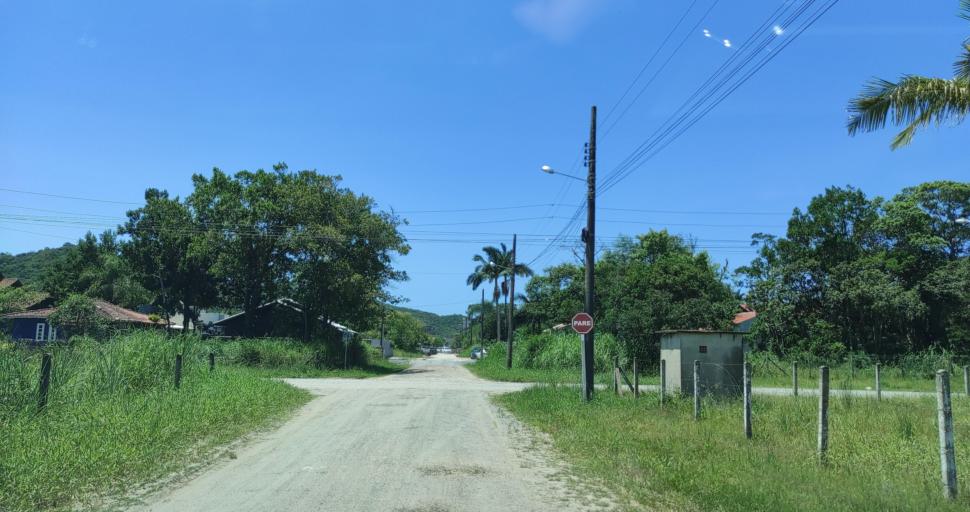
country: BR
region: Santa Catarina
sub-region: Porto Belo
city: Porto Belo
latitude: -27.1758
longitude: -48.5048
